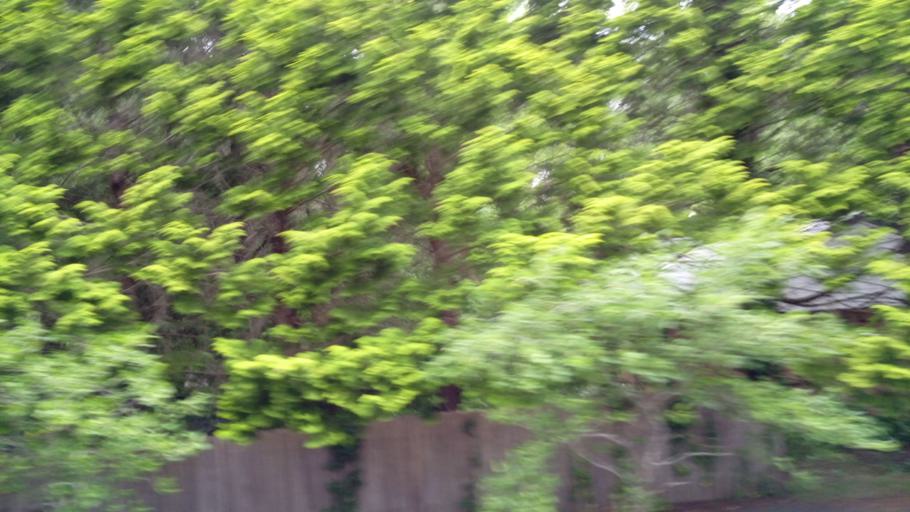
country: AU
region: New South Wales
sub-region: Blue Mountains Municipality
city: Leura
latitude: -33.7238
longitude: 150.3284
